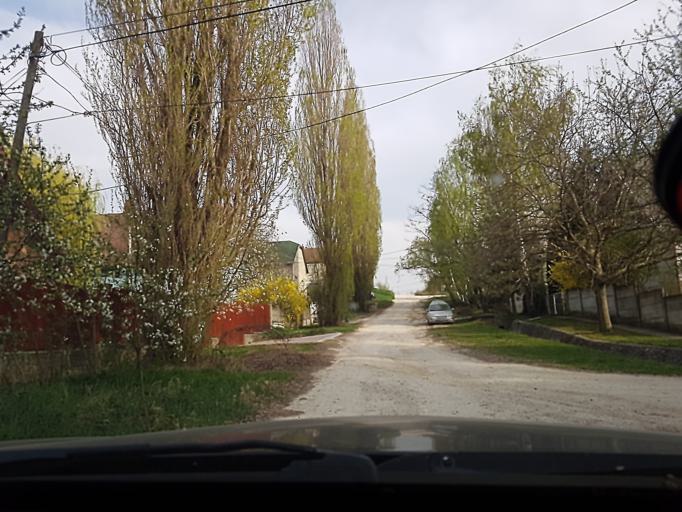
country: HU
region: Pest
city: Piliscsaba
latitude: 47.6385
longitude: 18.8242
